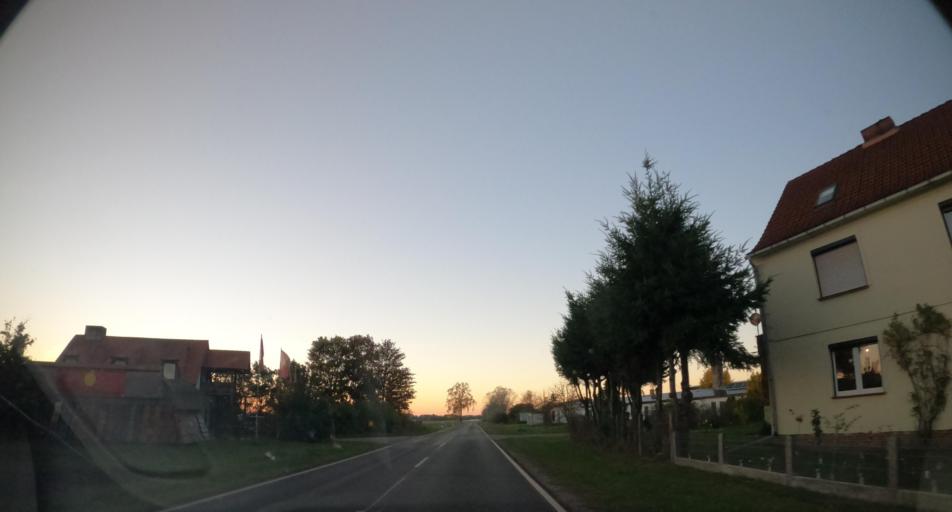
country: DE
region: Mecklenburg-Vorpommern
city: Ducherow
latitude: 53.7773
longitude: 13.8850
